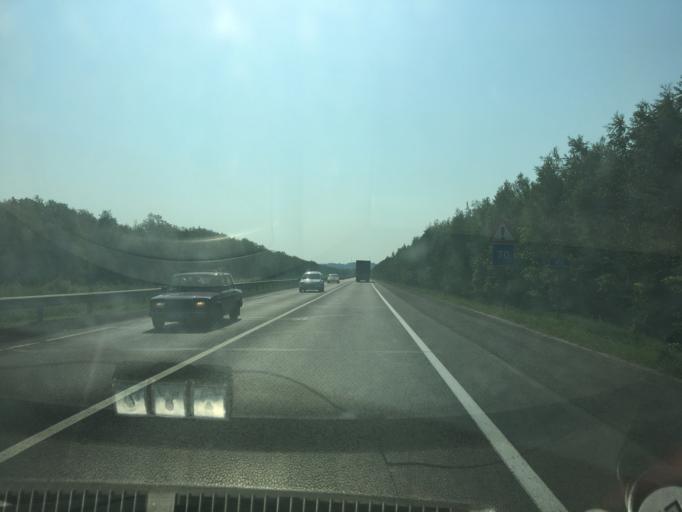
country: RU
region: Nizjnij Novgorod
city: Pamyat' Parizhskoy Kommuny
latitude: 56.0844
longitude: 44.3498
